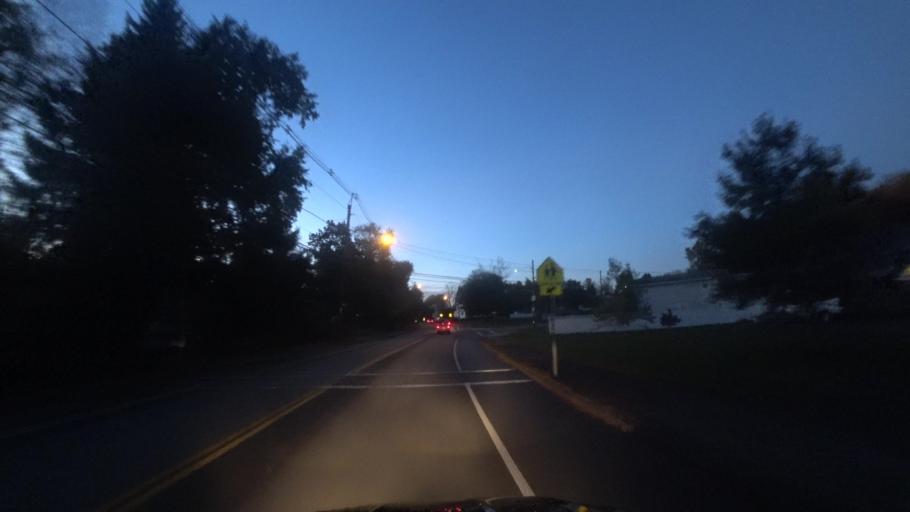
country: US
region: Massachusetts
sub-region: Middlesex County
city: Reading
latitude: 42.5444
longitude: -71.0898
